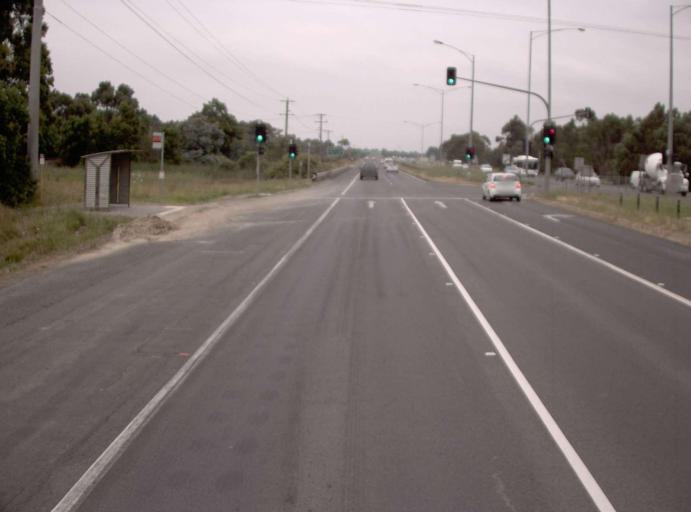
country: AU
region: Victoria
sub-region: Latrobe
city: Traralgon
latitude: -38.2205
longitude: 146.4723
